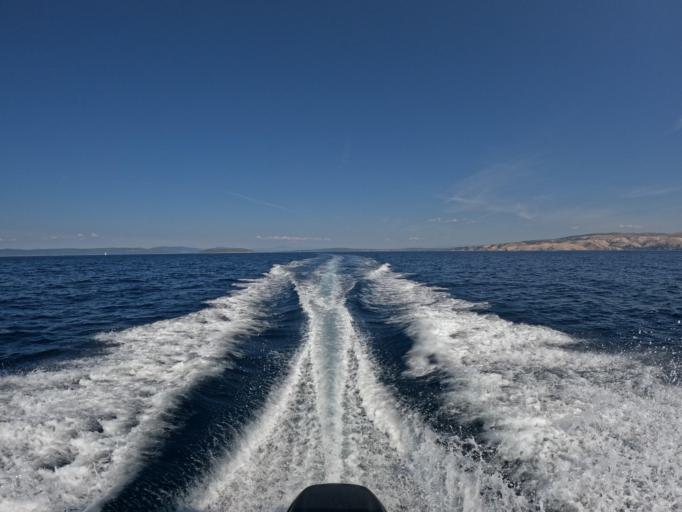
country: HR
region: Primorsko-Goranska
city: Punat
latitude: 44.9042
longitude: 14.6329
